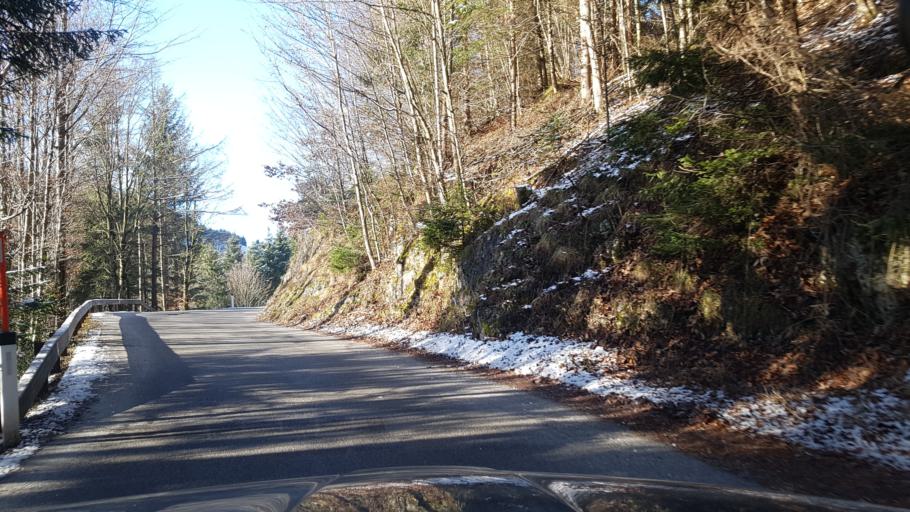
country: AT
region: Salzburg
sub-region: Politischer Bezirk Salzburg-Umgebung
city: Ebenau
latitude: 47.7756
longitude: 13.1664
